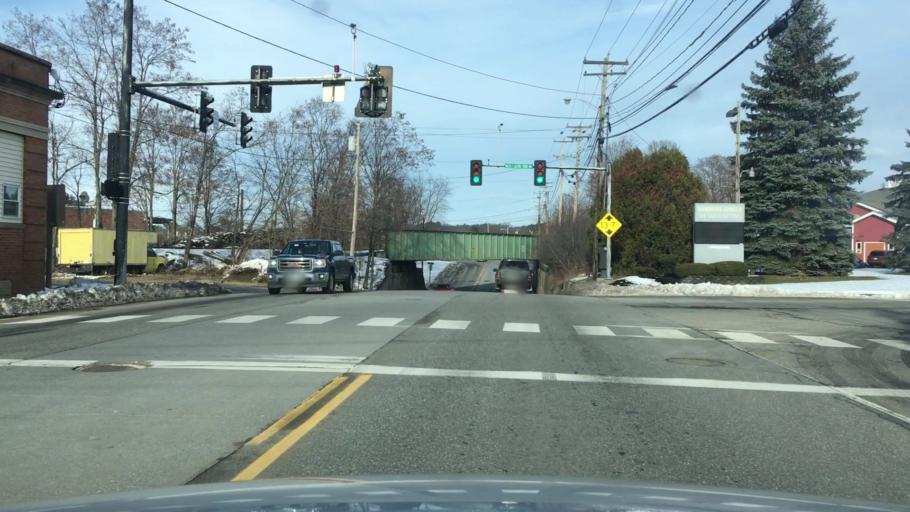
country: US
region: Maine
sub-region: Androscoggin County
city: Lewiston
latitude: 44.1235
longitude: -70.2017
